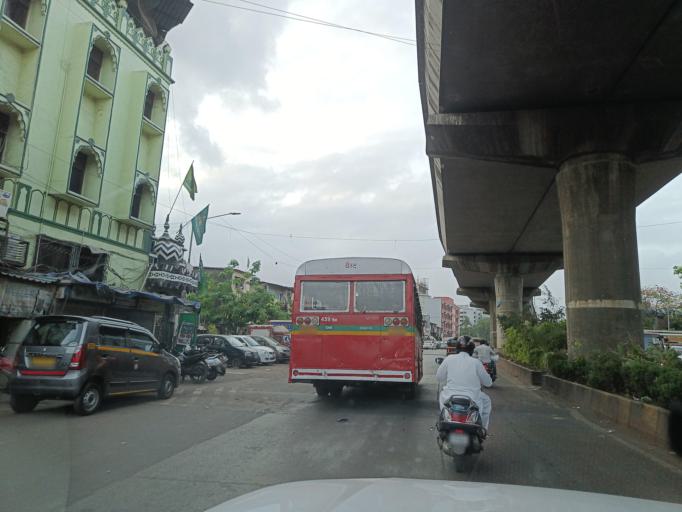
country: IN
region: Maharashtra
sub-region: Mumbai Suburban
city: Powai
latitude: 19.1014
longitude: 72.8908
